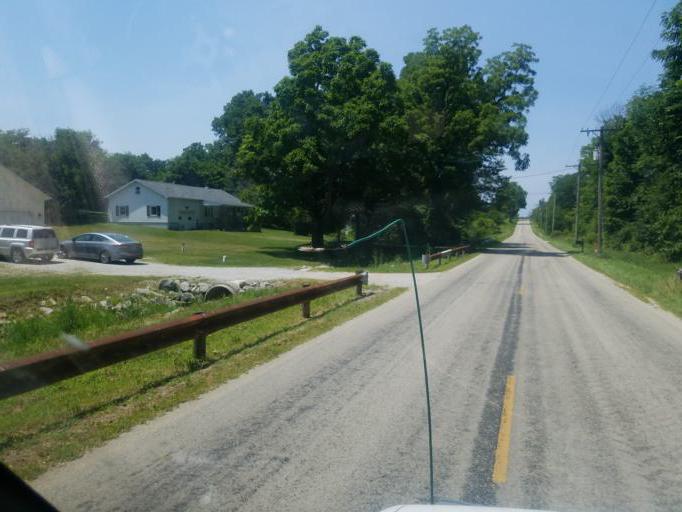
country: US
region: Ohio
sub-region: Shelby County
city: Sidney
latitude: 40.3057
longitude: -84.1033
